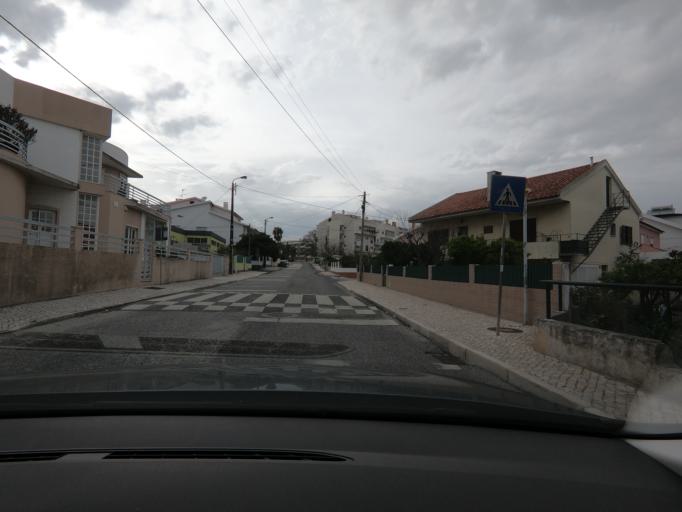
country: PT
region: Lisbon
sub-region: Cascais
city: Sao Domingos de Rana
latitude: 38.7114
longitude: -9.3340
